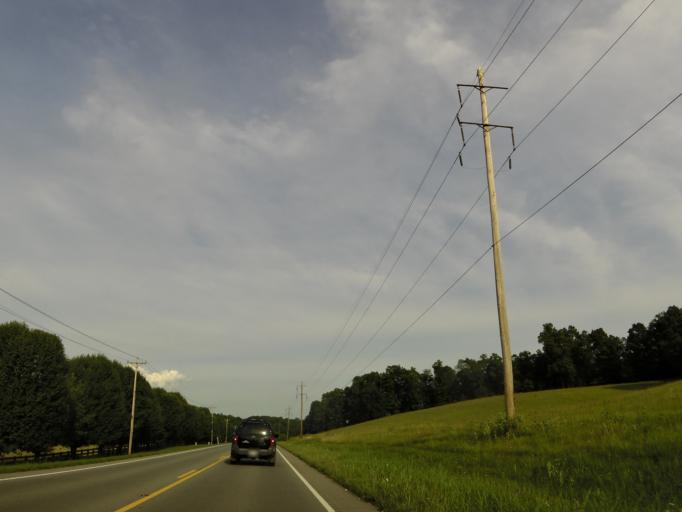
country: US
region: Tennessee
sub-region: Humphreys County
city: McEwen
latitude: 36.1012
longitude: -87.6101
